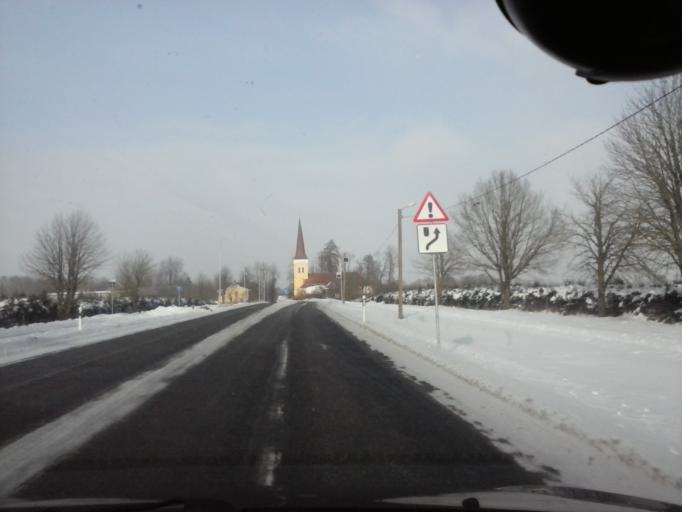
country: EE
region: Viljandimaa
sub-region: Abja vald
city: Abja-Paluoja
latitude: 58.3227
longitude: 25.3048
